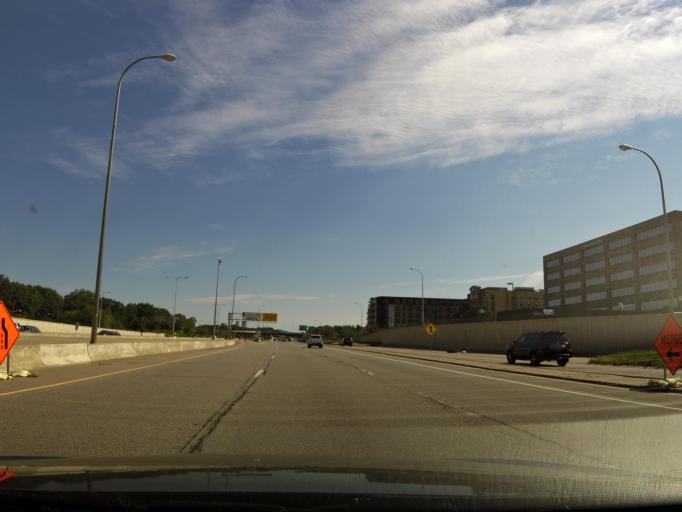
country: US
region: Minnesota
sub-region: Hennepin County
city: Saint Louis Park
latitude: 44.9703
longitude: -93.3499
